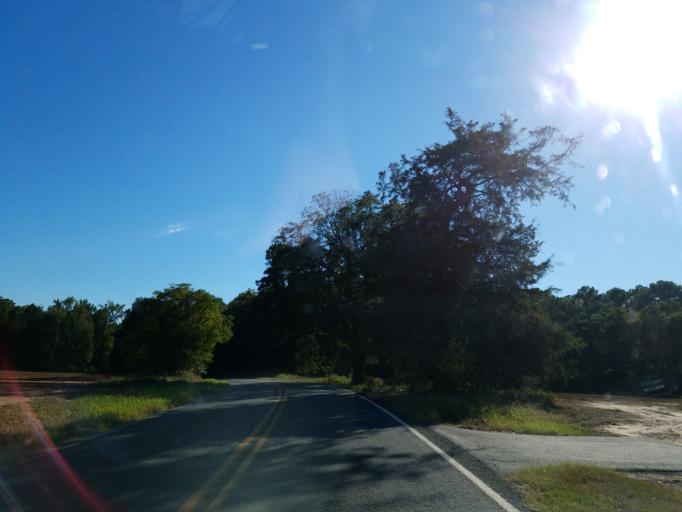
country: US
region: Georgia
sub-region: Dooly County
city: Unadilla
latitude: 32.2276
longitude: -83.8822
